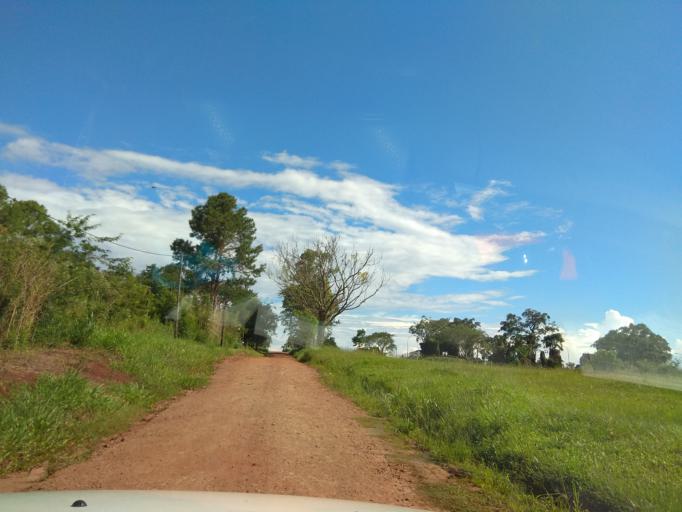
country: AR
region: Misiones
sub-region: Departamento de Candelaria
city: Candelaria
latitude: -27.4527
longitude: -55.7541
